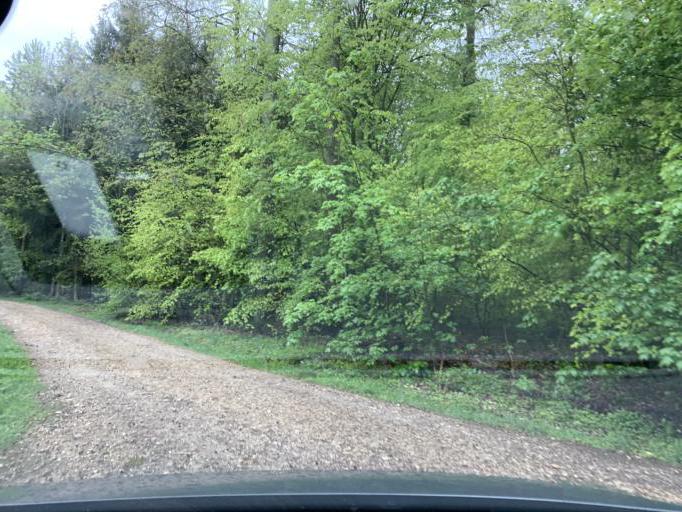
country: CH
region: Schaffhausen
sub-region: Bezirk Schaffhausen
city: Neuhausen
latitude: 47.6992
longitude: 8.6112
